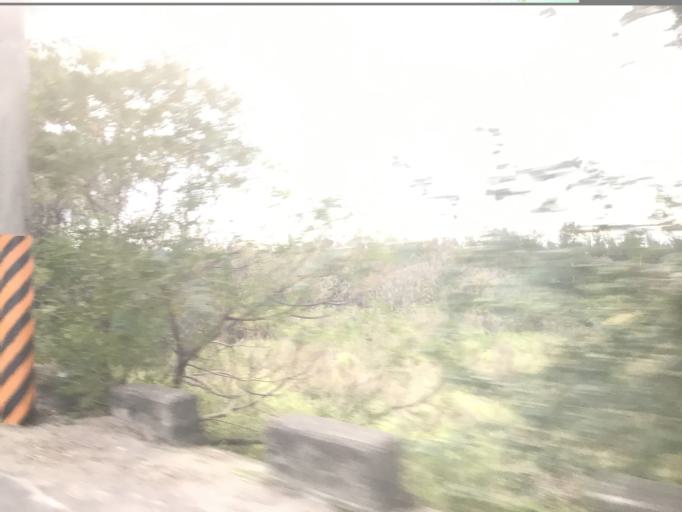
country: TW
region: Taiwan
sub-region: Hsinchu
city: Hsinchu
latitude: 24.7343
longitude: 120.8849
